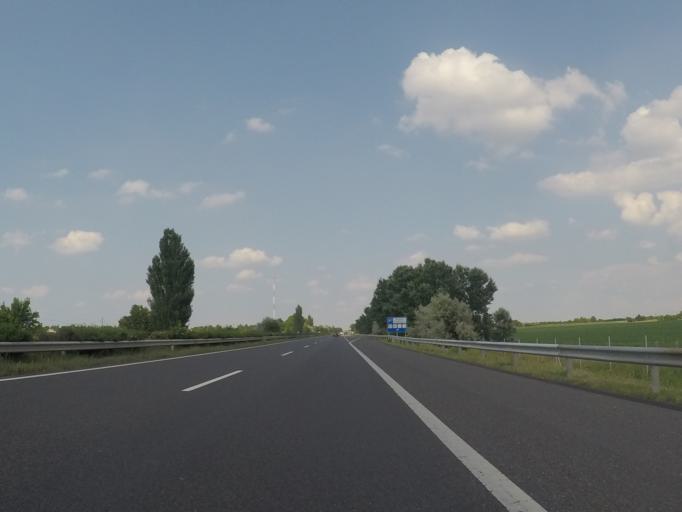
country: HU
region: Somogy
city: Siofok
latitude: 46.9125
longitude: 18.0988
